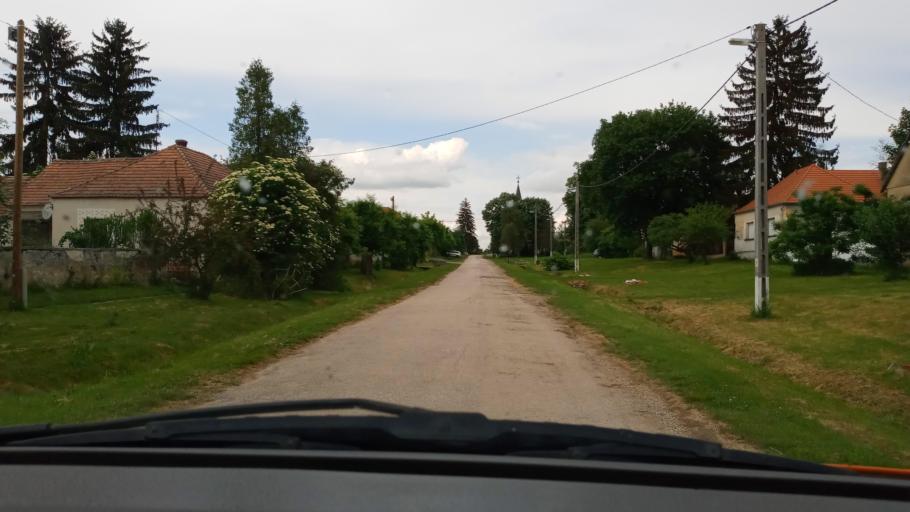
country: HU
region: Baranya
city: Harkany
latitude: 45.8976
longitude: 18.1365
